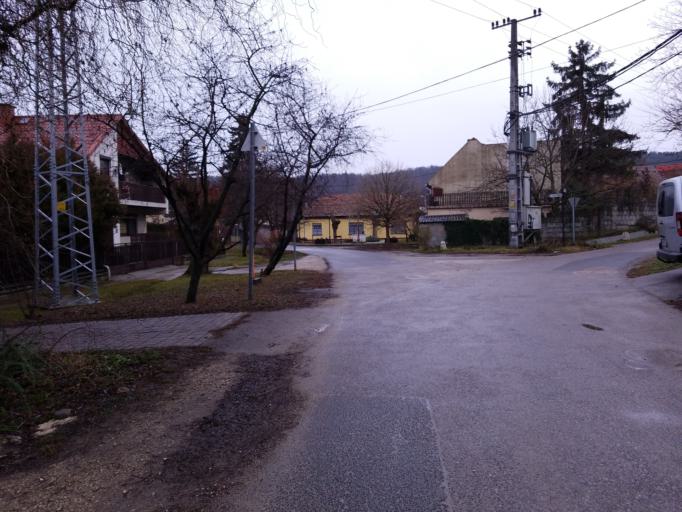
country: HU
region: Pest
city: Toeroekbalint
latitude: 47.4319
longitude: 18.9106
